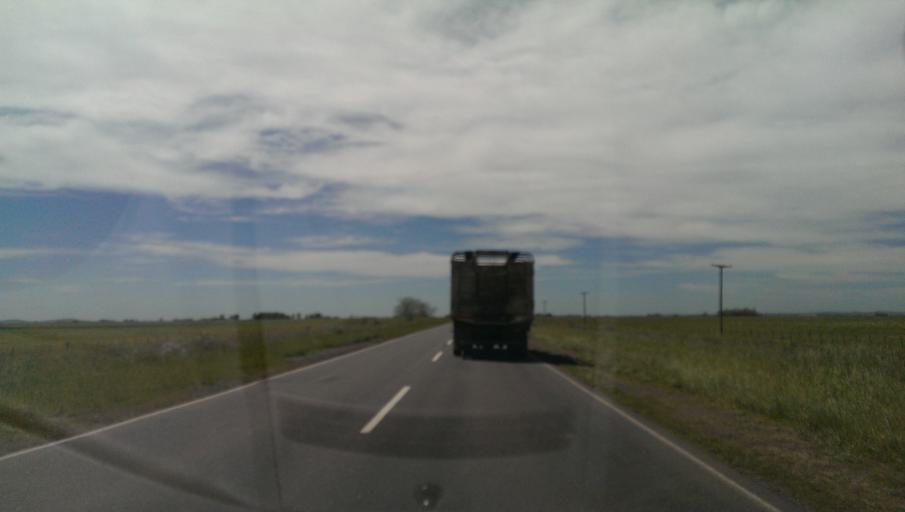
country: AR
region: Buenos Aires
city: Olavarria
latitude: -37.0584
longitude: -60.4566
